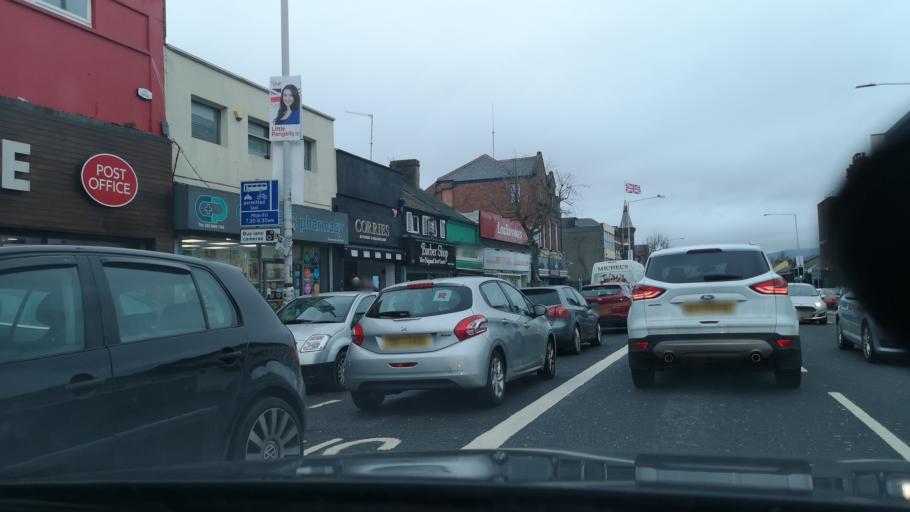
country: GB
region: Northern Ireland
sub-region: City of Belfast
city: Belfast
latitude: 54.5759
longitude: -5.9180
